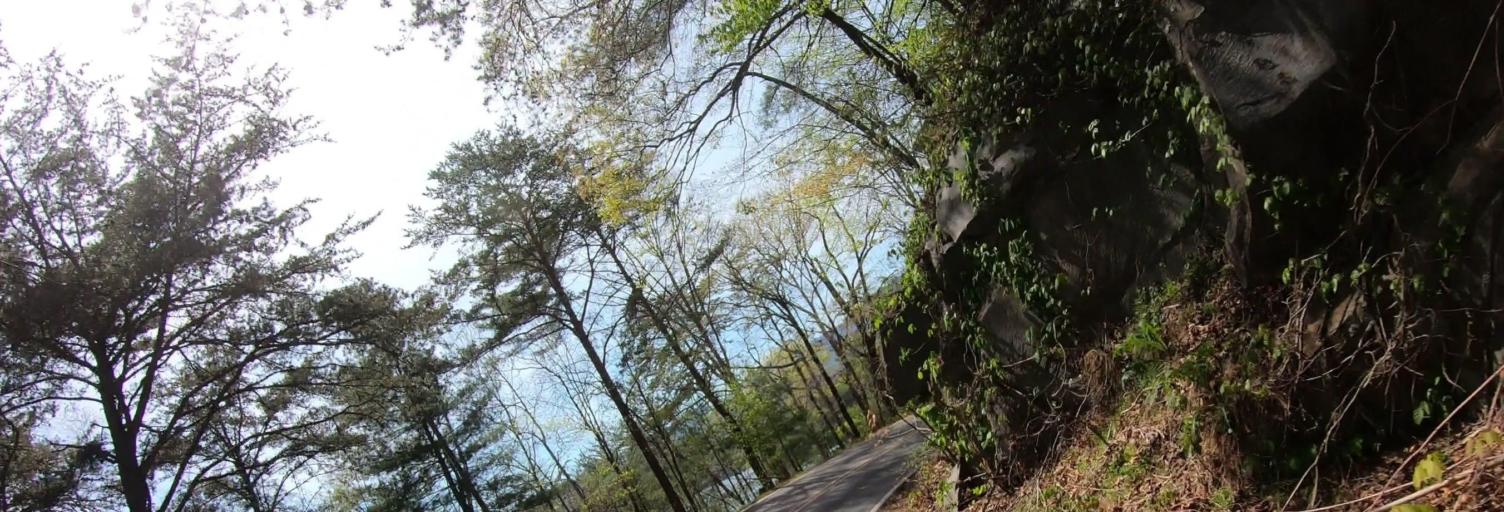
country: US
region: North Carolina
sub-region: Graham County
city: Robbinsville
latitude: 35.3676
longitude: -83.8673
